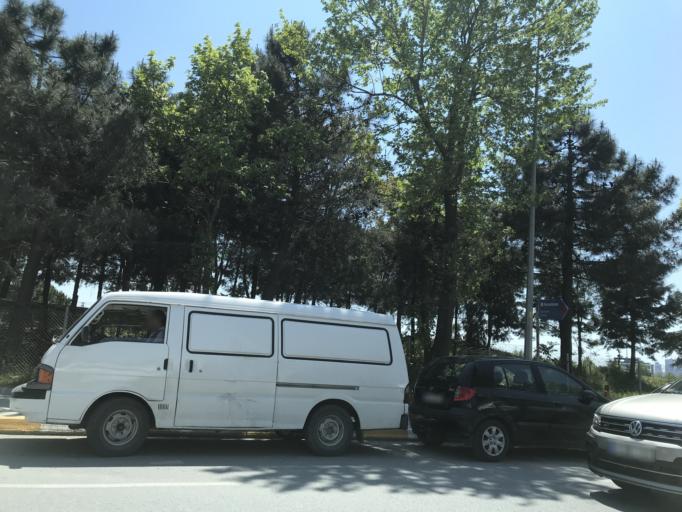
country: TR
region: Istanbul
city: Esenyurt
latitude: 41.0554
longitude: 28.6731
